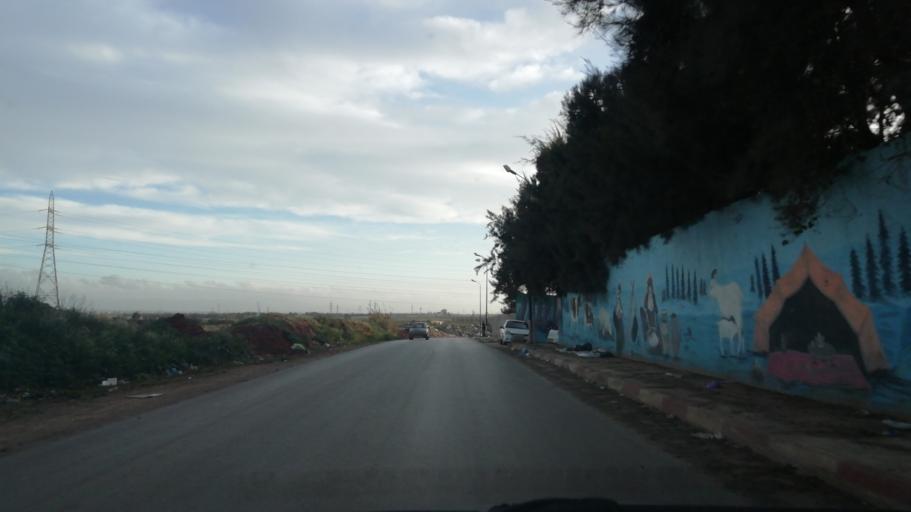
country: DZ
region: Oran
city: Es Senia
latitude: 35.6797
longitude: -0.5864
